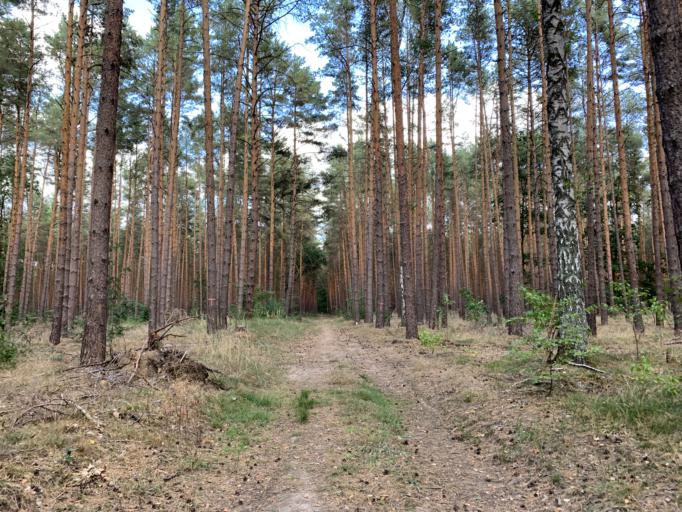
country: DE
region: Brandenburg
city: Michendorf
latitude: 52.3148
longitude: 13.0048
